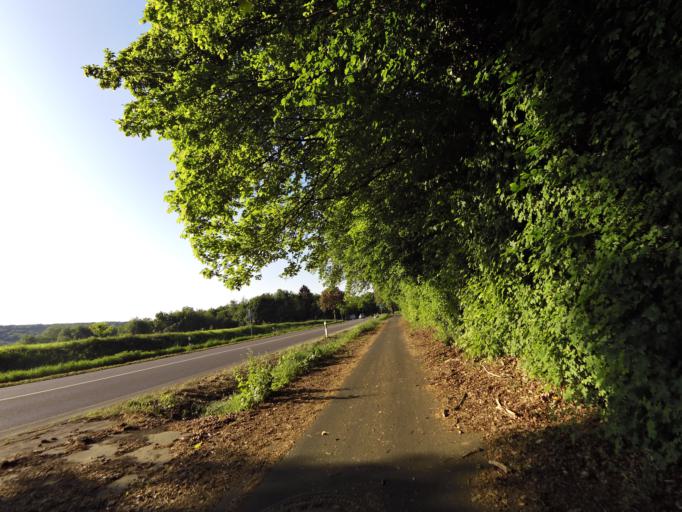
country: DE
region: North Rhine-Westphalia
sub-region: Regierungsbezirk Koln
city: Bonn
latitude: 50.6926
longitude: 7.0712
